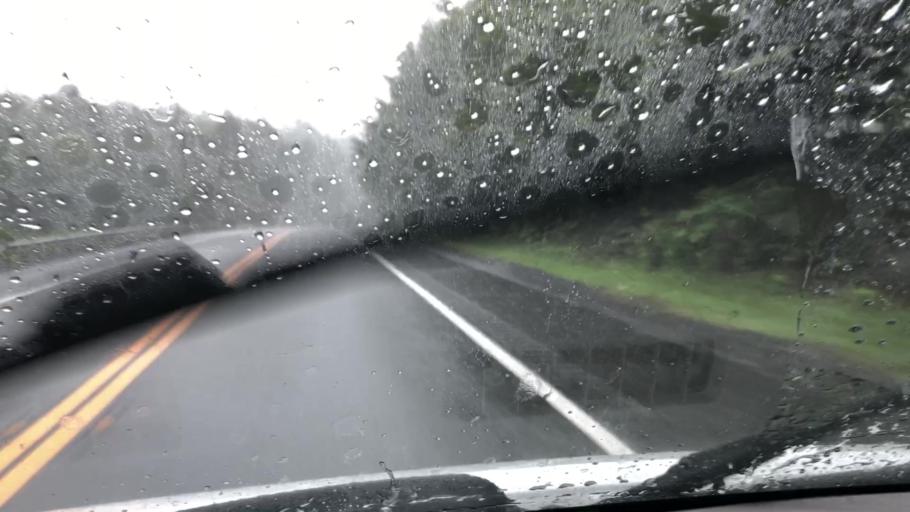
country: US
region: Massachusetts
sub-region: Hampshire County
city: Chesterfield
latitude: 42.4490
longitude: -72.8158
